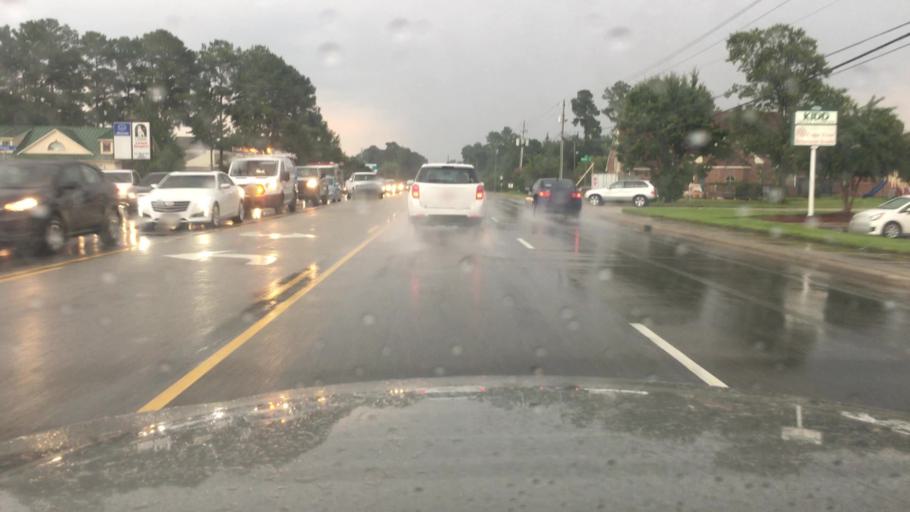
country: US
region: North Carolina
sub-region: Cumberland County
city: Fort Bragg
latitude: 35.0598
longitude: -79.0110
